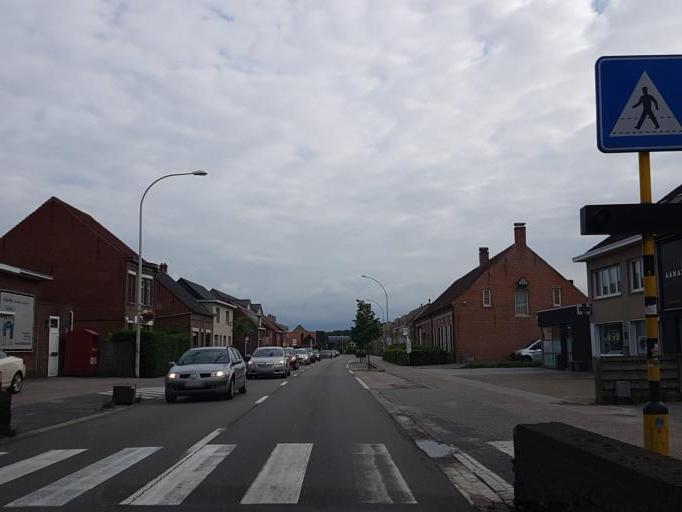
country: BE
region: Flanders
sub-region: Provincie Antwerpen
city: Zoersel
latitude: 51.2652
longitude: 4.7124
